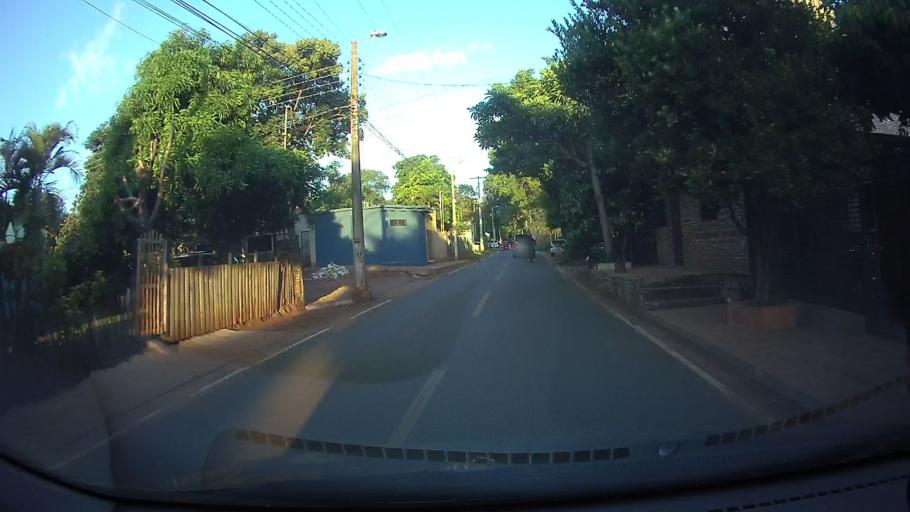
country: PY
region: Central
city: San Lorenzo
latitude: -25.2865
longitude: -57.5100
